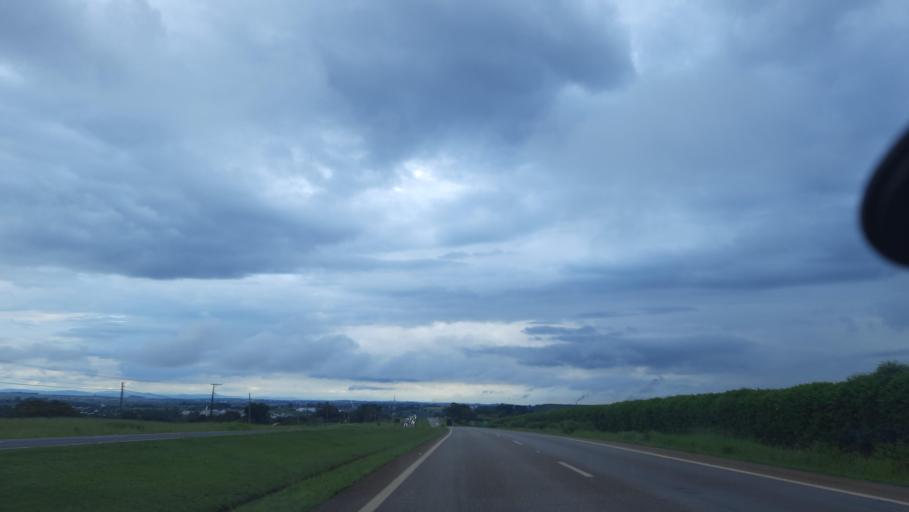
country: BR
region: Sao Paulo
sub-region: Moji-Guacu
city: Mogi-Gaucu
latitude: -22.2565
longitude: -46.9771
